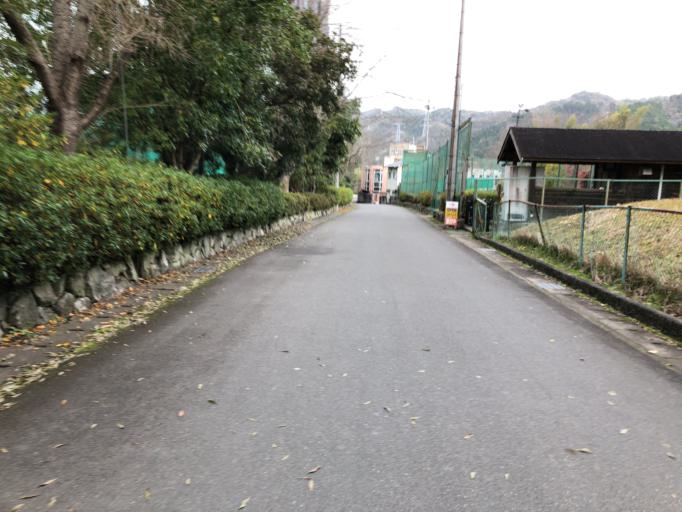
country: JP
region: Kyoto
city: Kameoka
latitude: 34.9909
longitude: 135.6227
